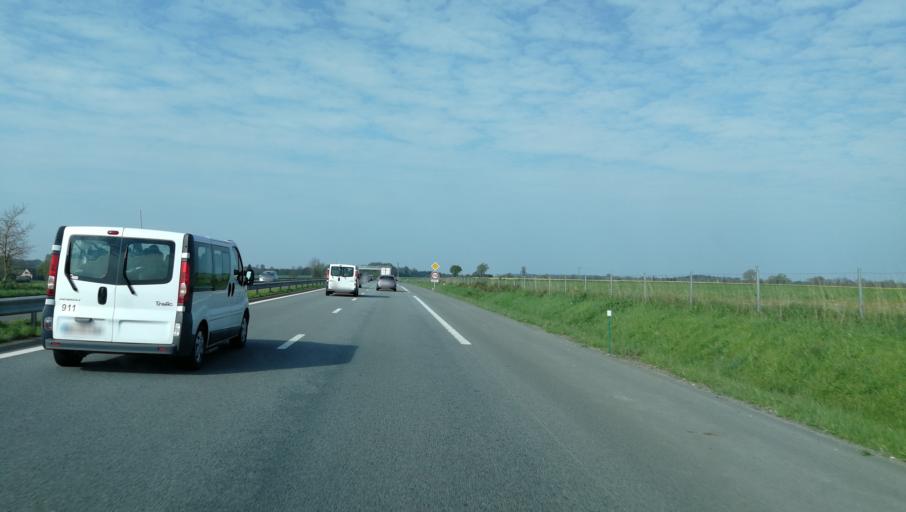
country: FR
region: Brittany
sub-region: Departement d'Ille-et-Vilaine
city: Erbree
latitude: 48.0871
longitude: -1.1161
